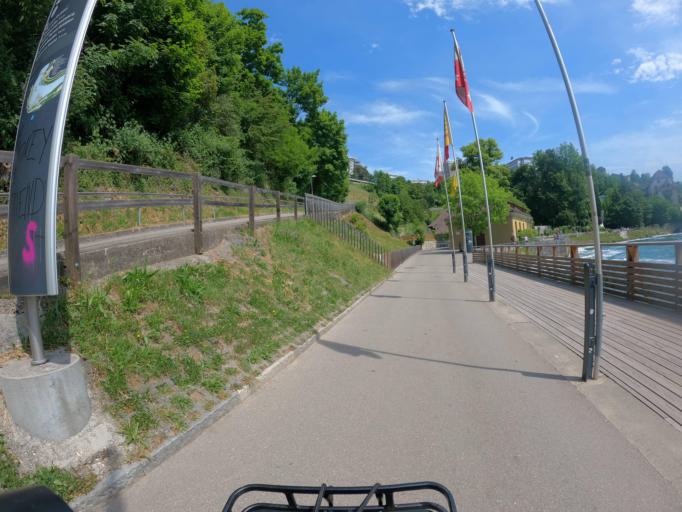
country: CH
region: Schaffhausen
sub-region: Bezirk Schaffhausen
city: Neuhausen
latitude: 47.6799
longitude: 8.6135
